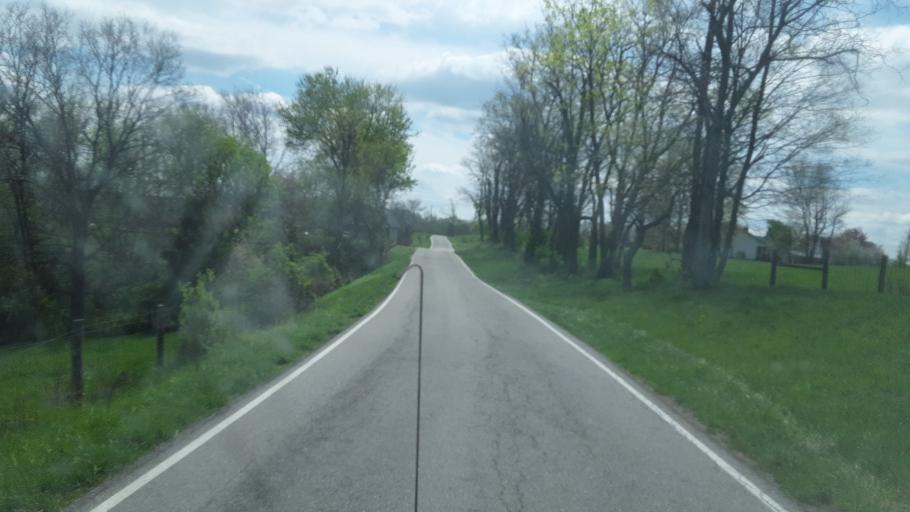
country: US
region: Kentucky
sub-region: Owen County
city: Owenton
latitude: 38.6529
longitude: -84.7722
